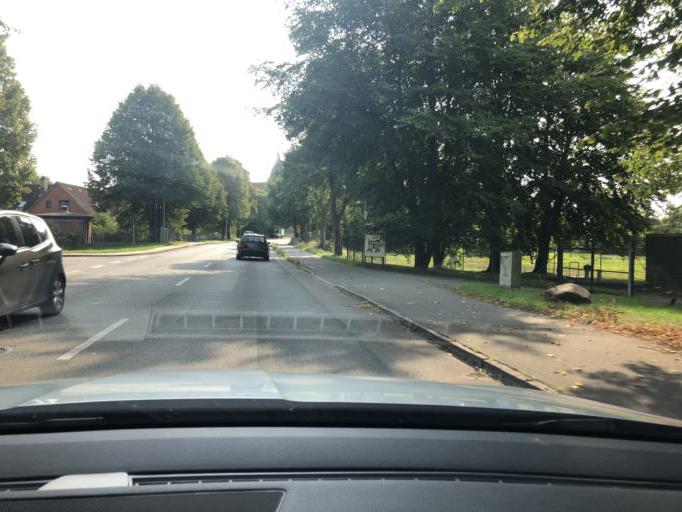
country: DE
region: Schleswig-Holstein
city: Gross Gronau
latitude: 53.7996
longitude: 10.7519
